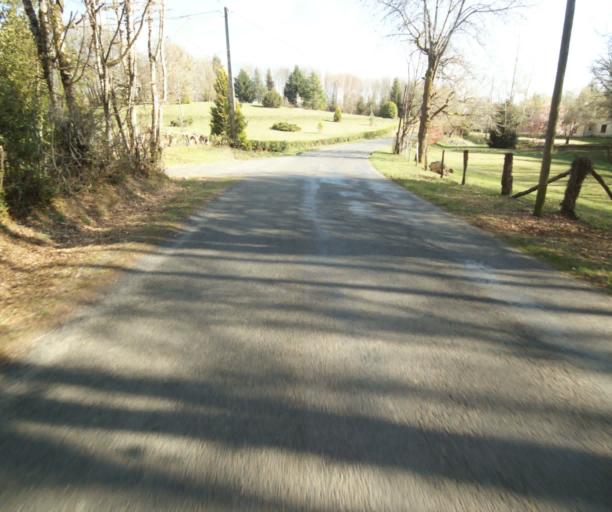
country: FR
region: Limousin
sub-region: Departement de la Correze
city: Saint-Mexant
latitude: 45.3310
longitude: 1.6241
